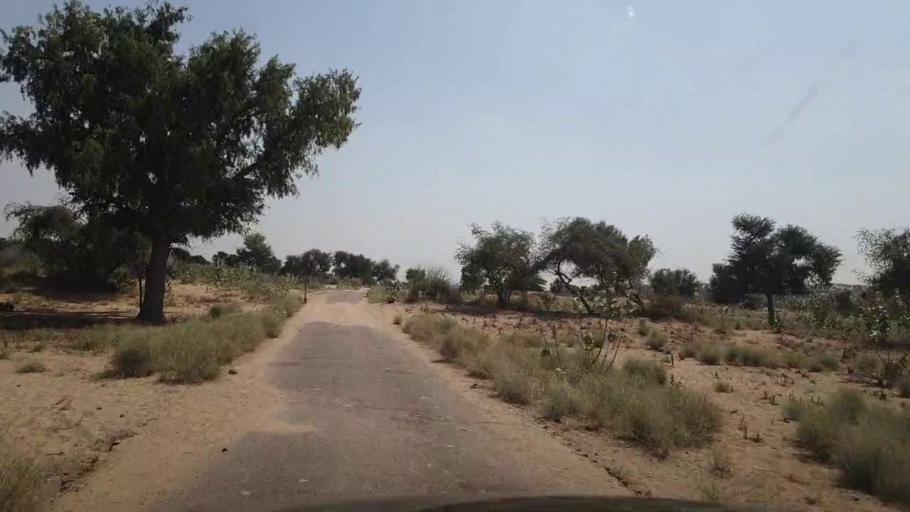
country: PK
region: Sindh
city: Islamkot
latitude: 25.0850
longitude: 70.6744
